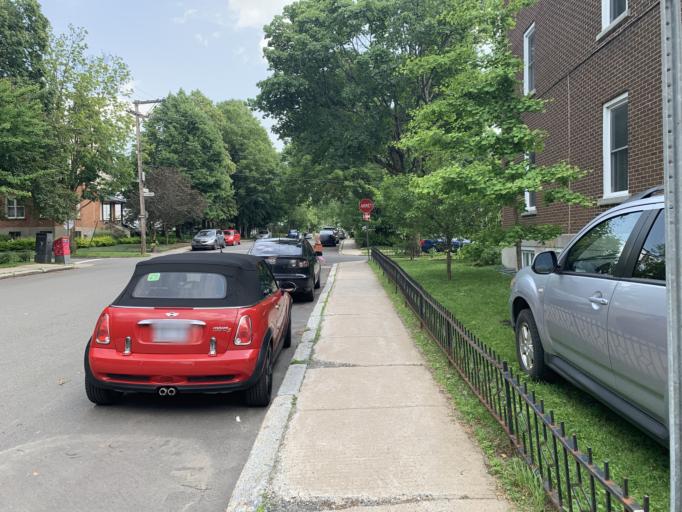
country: CA
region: Quebec
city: Quebec
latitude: 46.8002
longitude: -71.2327
